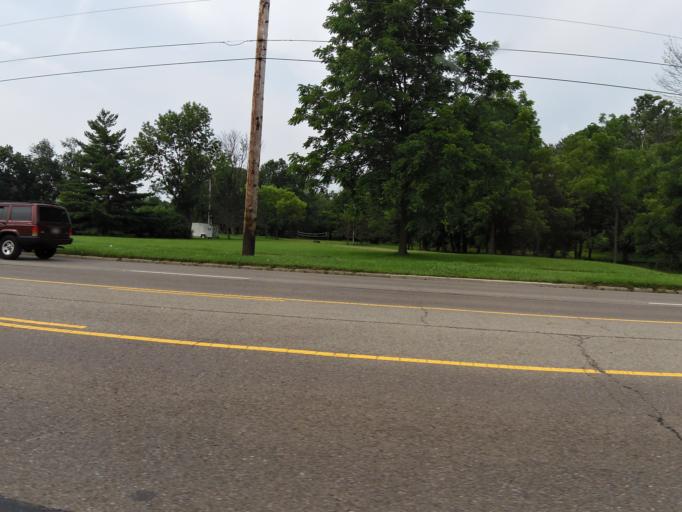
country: US
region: Ohio
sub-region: Greene County
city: Bellbrook
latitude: 39.6724
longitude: -84.1137
